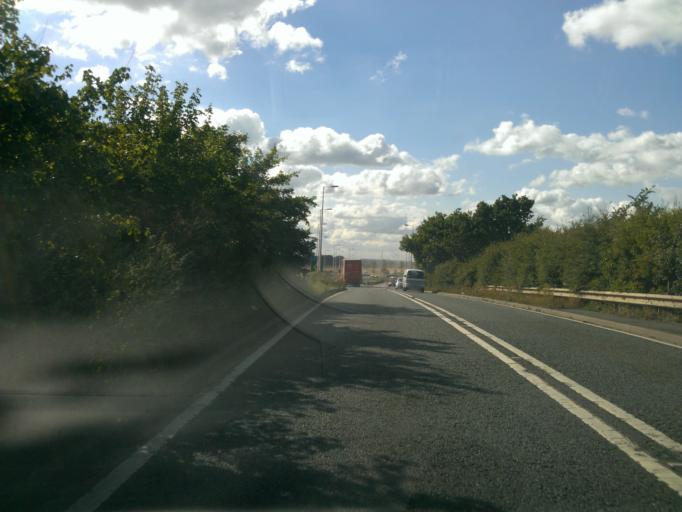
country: GB
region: England
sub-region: Warwickshire
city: Nuneaton
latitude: 52.5516
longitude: -1.4600
